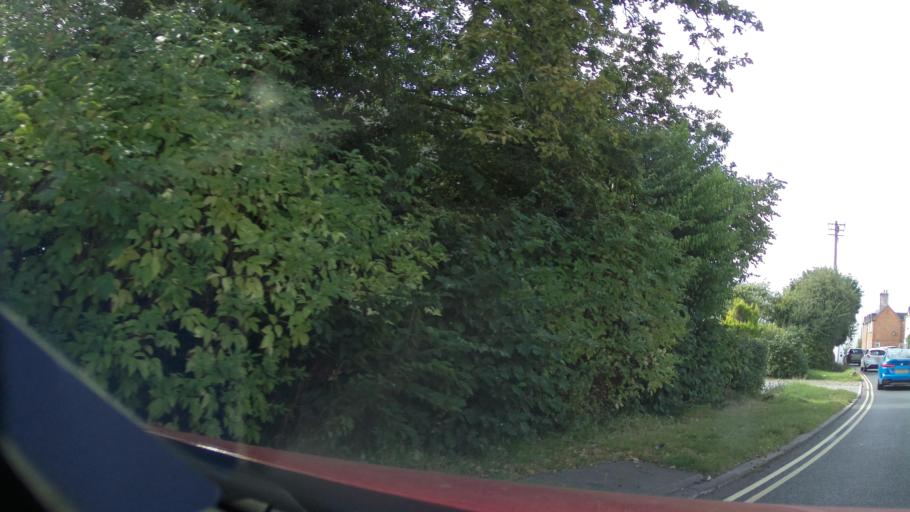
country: GB
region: England
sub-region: Derbyshire
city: Little Eaton
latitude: 52.9533
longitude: -1.4866
